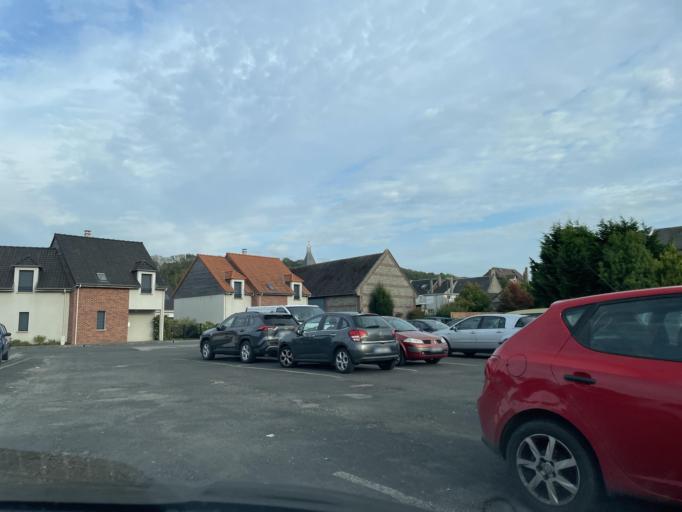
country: FR
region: Haute-Normandie
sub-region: Departement de la Seine-Maritime
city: Criel-sur-Mer
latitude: 50.0172
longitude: 1.3167
